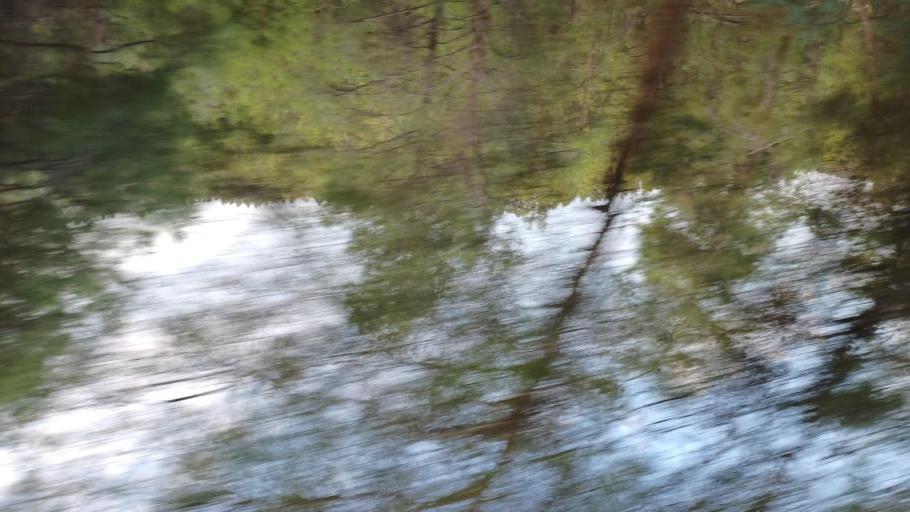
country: CY
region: Lefkosia
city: Kakopetria
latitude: 35.0523
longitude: 32.9085
